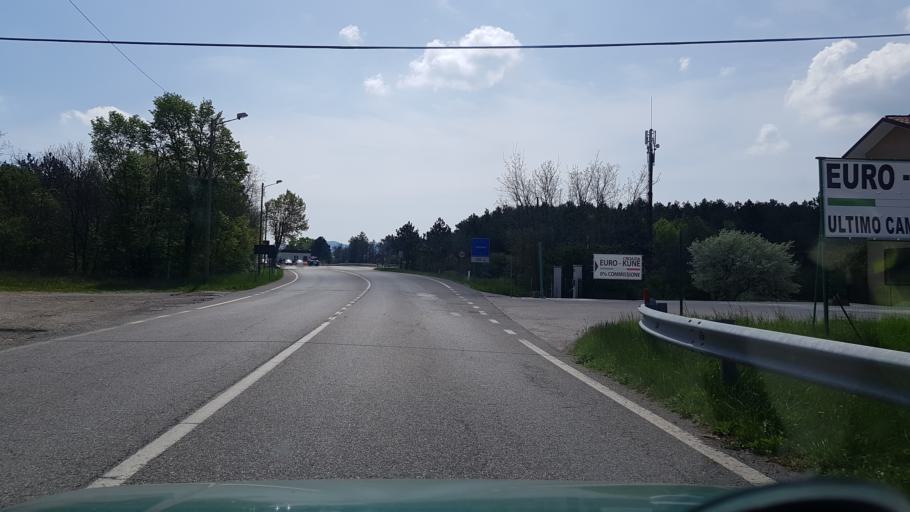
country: SI
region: Hrpelje-Kozina
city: Kozina
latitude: 45.6251
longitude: 13.9002
